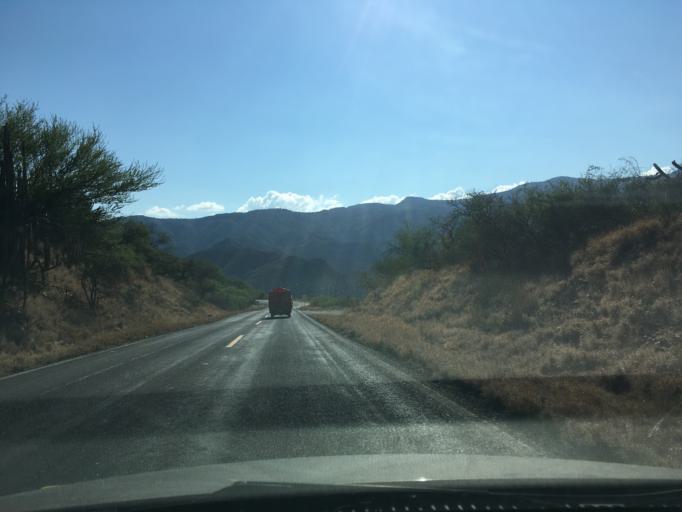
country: MX
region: Hidalgo
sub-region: San Agustin Metzquititlan
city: Mezquititlan
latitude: 20.4641
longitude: -98.6752
